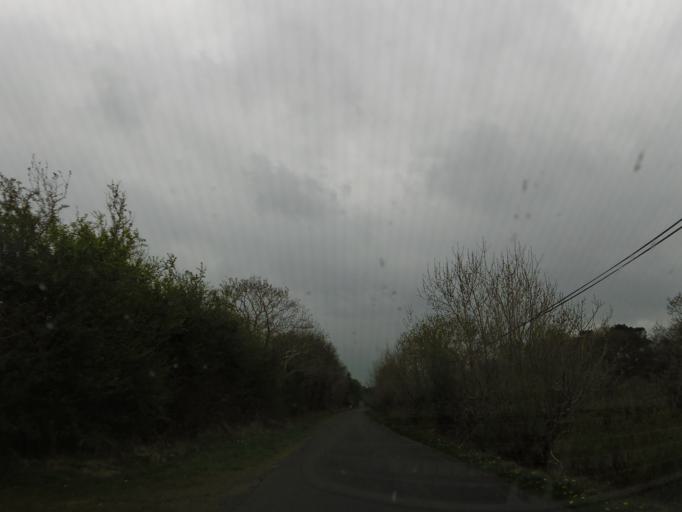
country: IE
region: Connaught
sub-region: Maigh Eo
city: Claremorris
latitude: 53.7829
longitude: -8.9608
